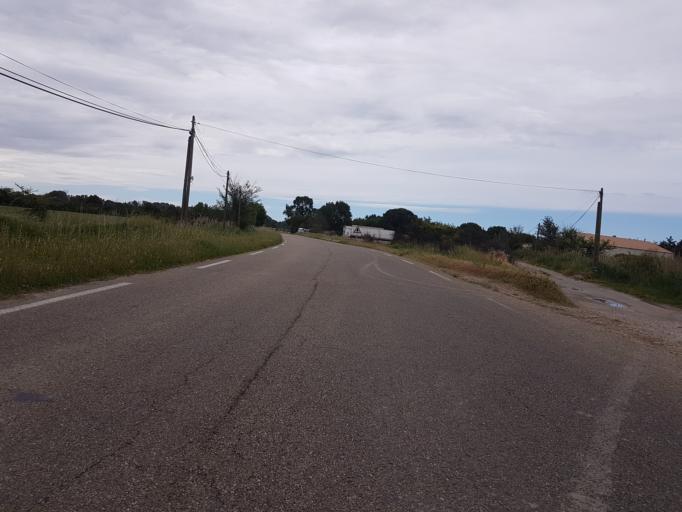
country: FR
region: Languedoc-Roussillon
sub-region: Departement du Gard
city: Saint-Gilles
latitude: 43.6666
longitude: 4.4407
